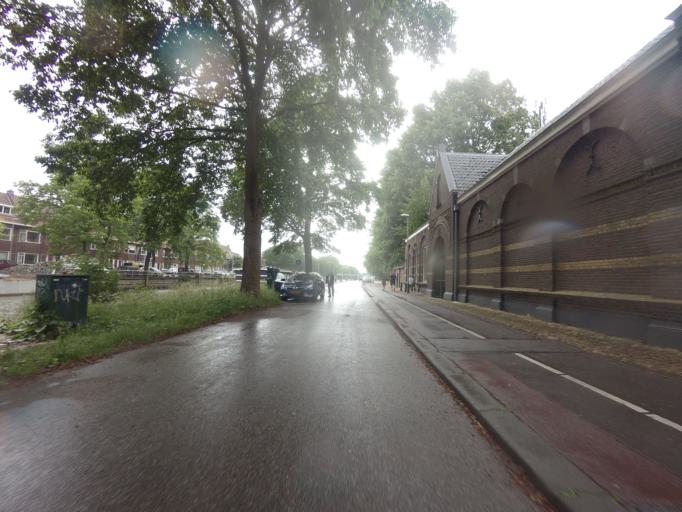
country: NL
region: Utrecht
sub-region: Gemeente Utrecht
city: Utrecht
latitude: 52.1089
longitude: 5.1055
